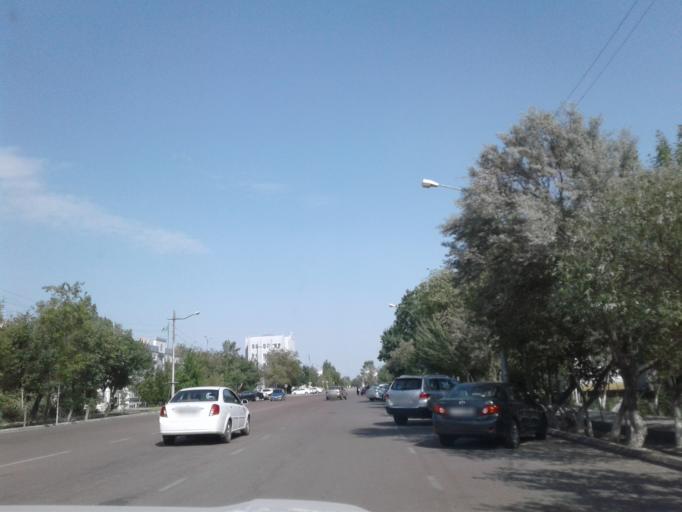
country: TM
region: Dasoguz
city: Dasoguz
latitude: 41.8312
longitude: 59.9592
